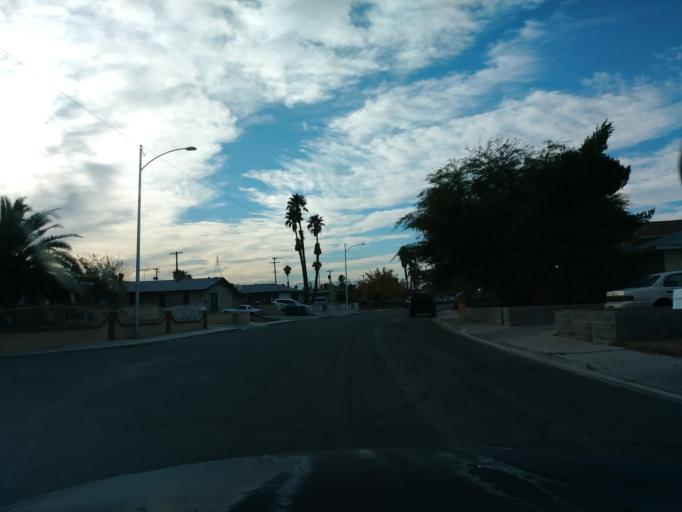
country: US
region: Nevada
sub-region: Clark County
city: Spring Valley
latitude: 36.1694
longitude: -115.2279
